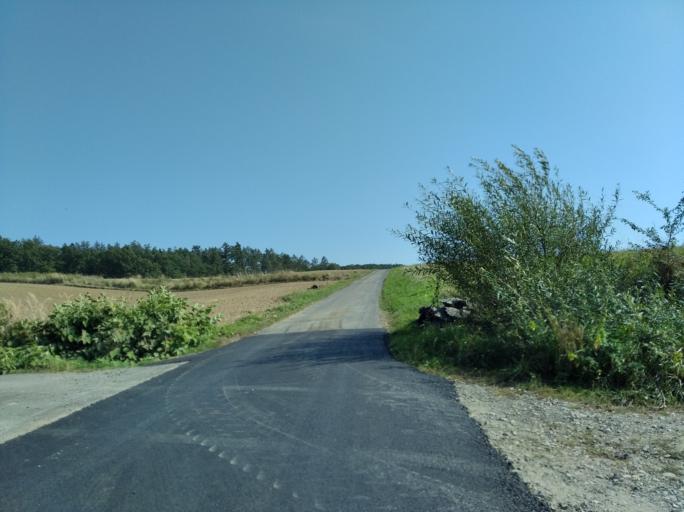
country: PL
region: Subcarpathian Voivodeship
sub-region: Powiat strzyzowski
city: Czudec
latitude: 49.9424
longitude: 21.8541
